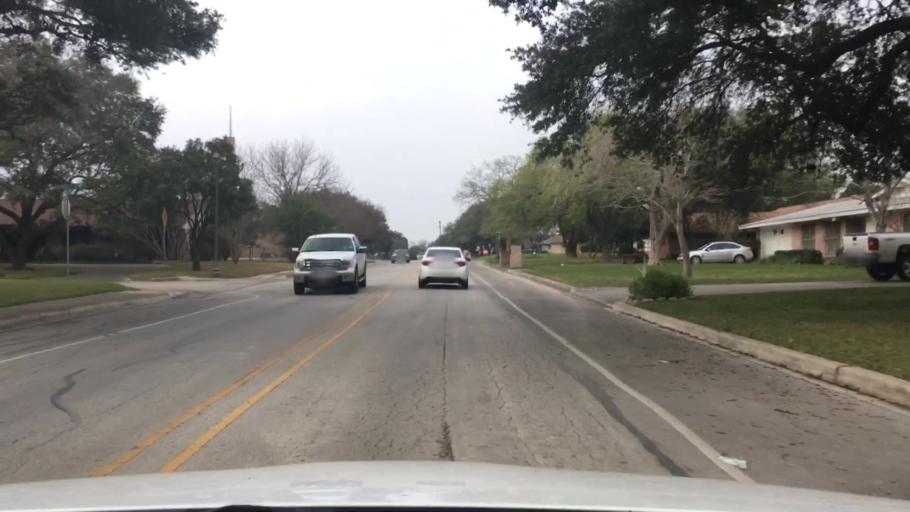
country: US
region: Texas
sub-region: Bexar County
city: Windcrest
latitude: 29.5208
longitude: -98.3816
